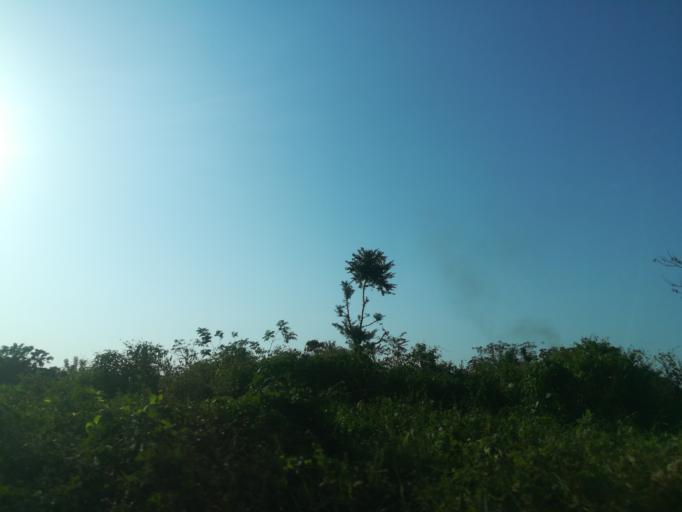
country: NG
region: Ogun
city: Abeokuta
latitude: 7.1893
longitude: 3.2836
